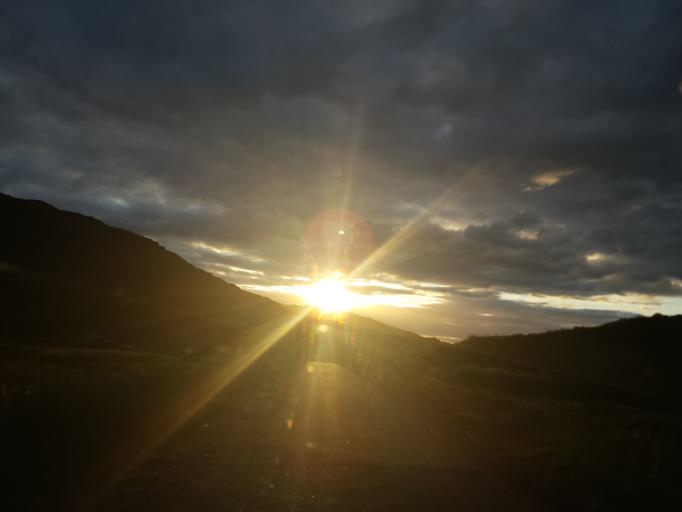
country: GB
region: Scotland
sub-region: Highland
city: Ullapool
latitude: 57.4725
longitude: -5.5901
